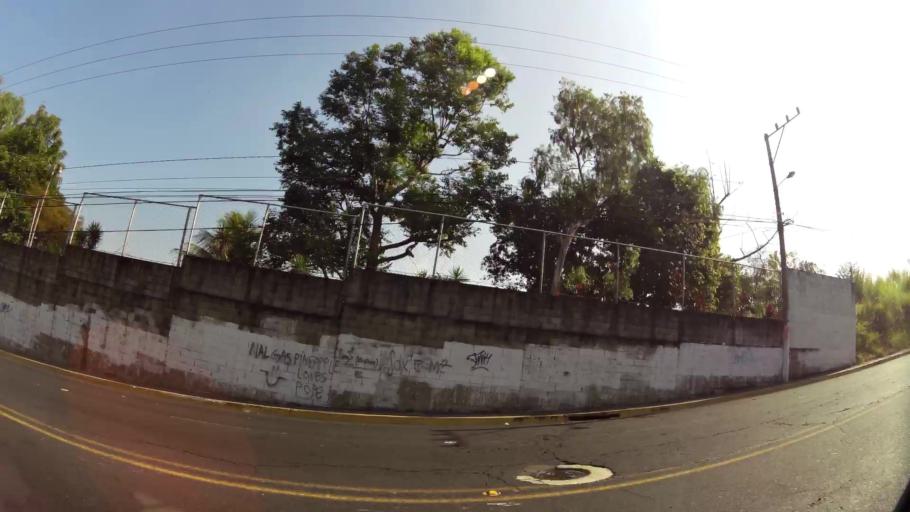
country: SV
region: La Libertad
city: Antiguo Cuscatlan
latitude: 13.6708
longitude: -89.2286
